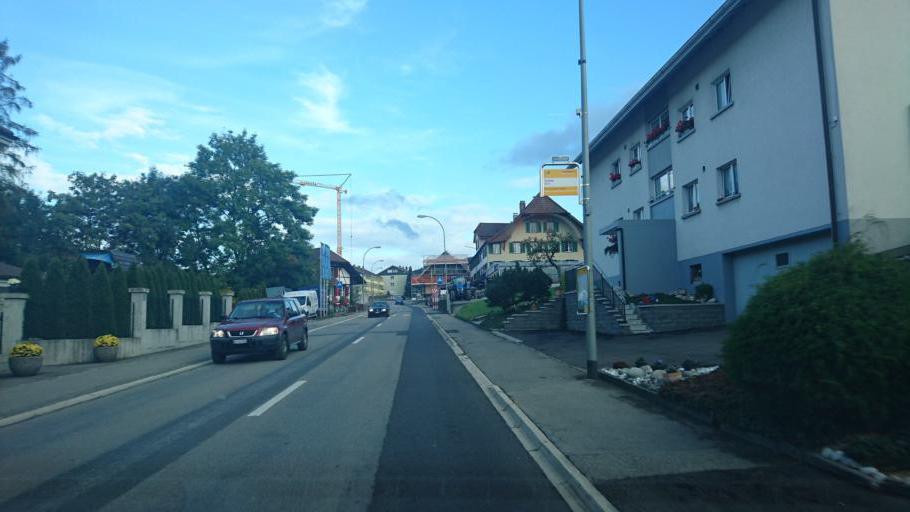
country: CH
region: Bern
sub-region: Bern-Mittelland District
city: Biglen
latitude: 46.9268
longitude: 7.6229
